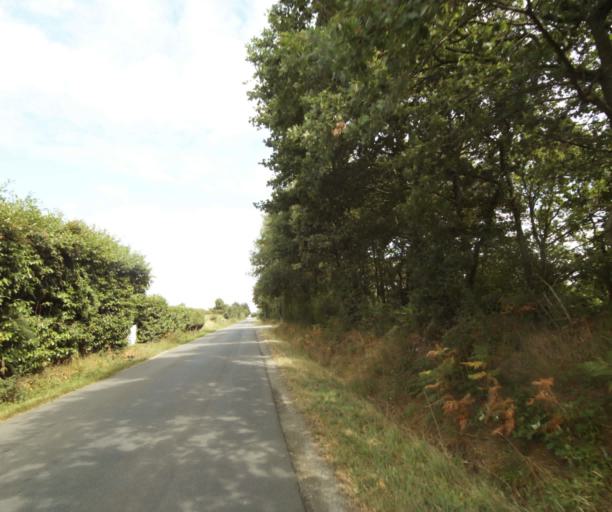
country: FR
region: Pays de la Loire
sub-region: Departement de la Sarthe
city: Sable-sur-Sarthe
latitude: 47.8166
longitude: -0.3167
